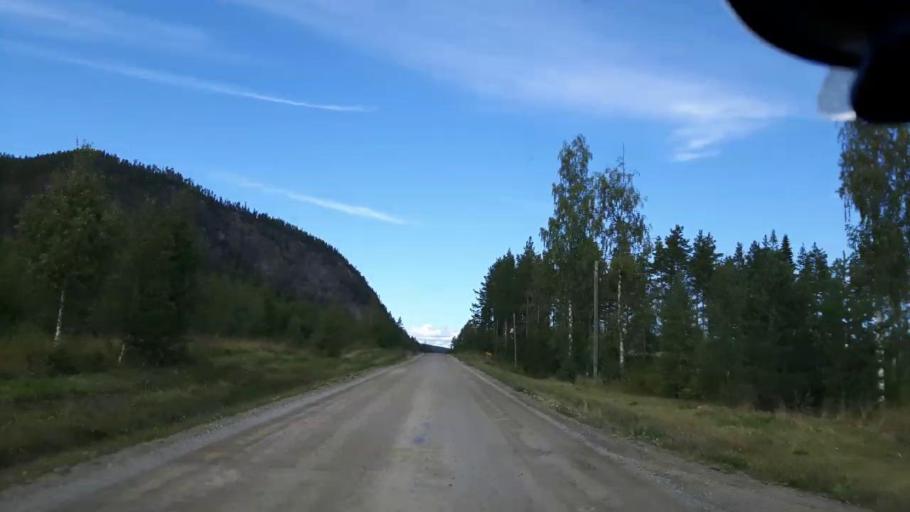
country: SE
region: Jaemtland
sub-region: Ragunda Kommun
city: Hammarstrand
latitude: 63.1278
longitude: 16.3251
